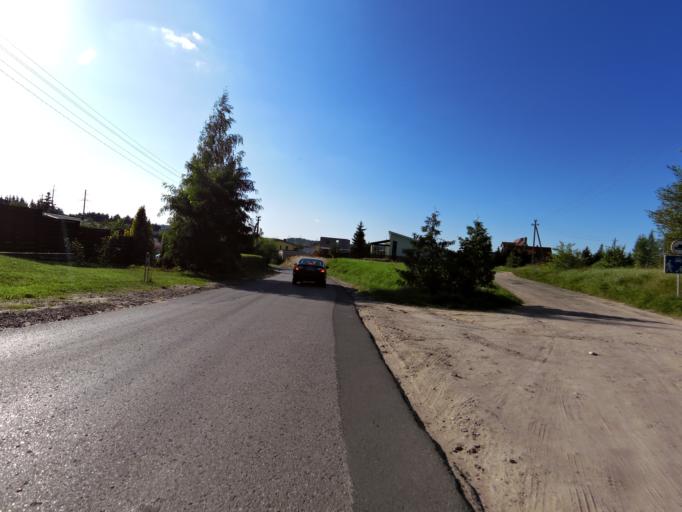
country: LT
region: Vilnius County
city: Pasilaiciai
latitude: 54.7308
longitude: 25.1891
